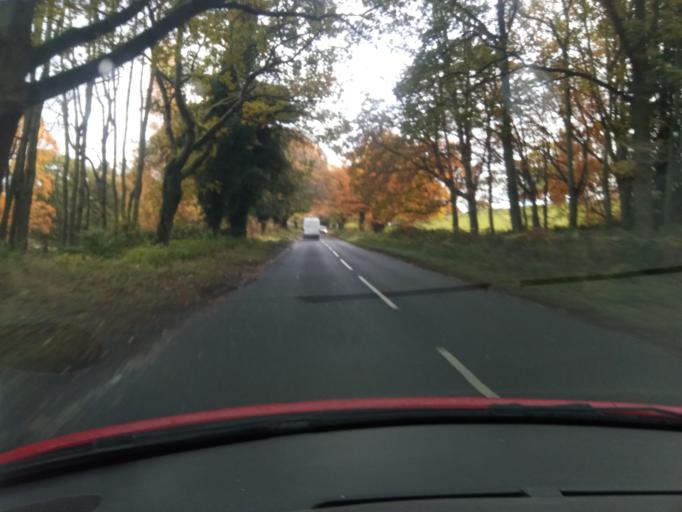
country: GB
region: England
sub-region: Northumberland
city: Birtley
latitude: 55.0687
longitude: -2.1957
